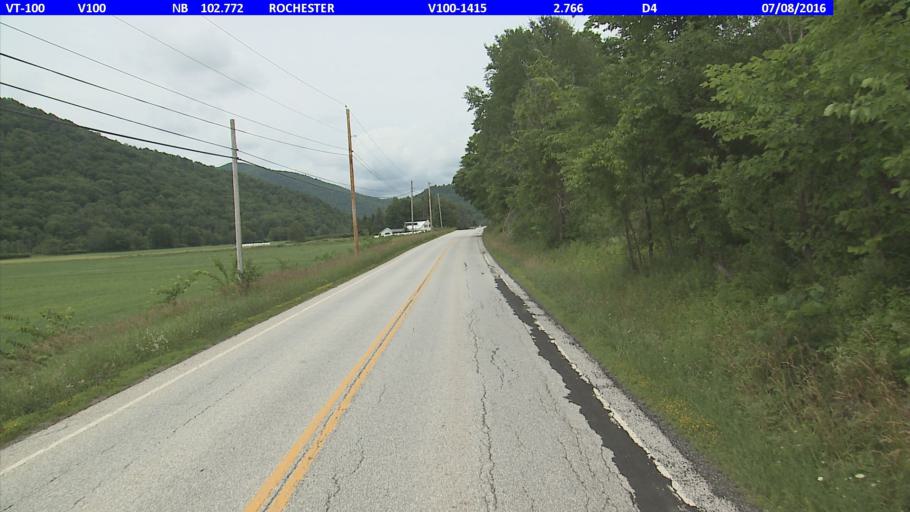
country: US
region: Vermont
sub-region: Orange County
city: Randolph
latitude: 43.8417
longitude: -72.7975
